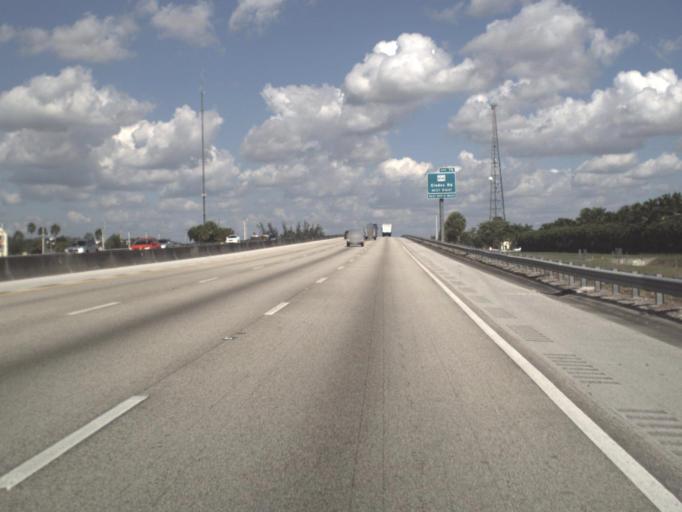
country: US
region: Florida
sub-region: Palm Beach County
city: Boca Del Mar
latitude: 26.3635
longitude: -80.1706
